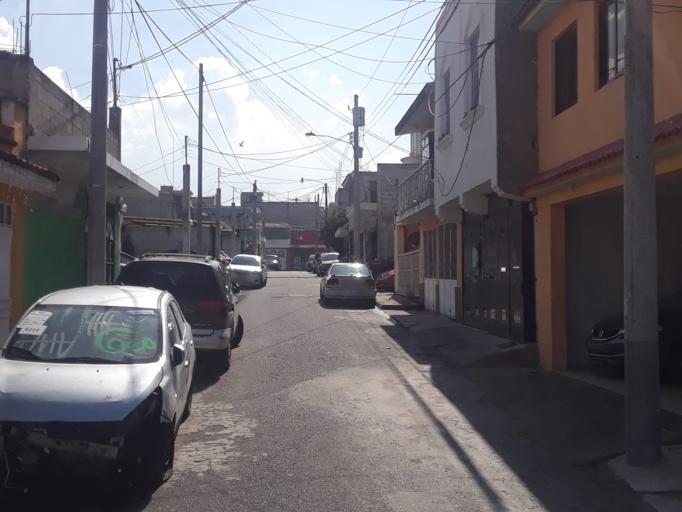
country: GT
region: Guatemala
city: Petapa
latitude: 14.5361
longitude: -90.5549
